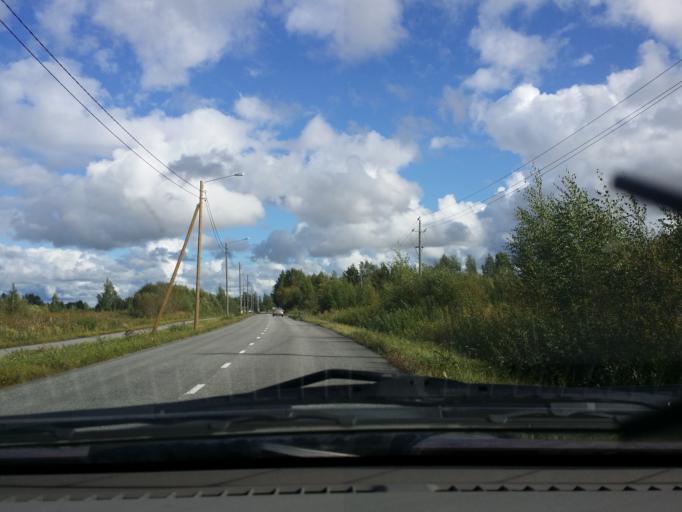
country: FI
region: Satakunta
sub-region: Pori
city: Pori
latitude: 61.4940
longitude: 21.8308
